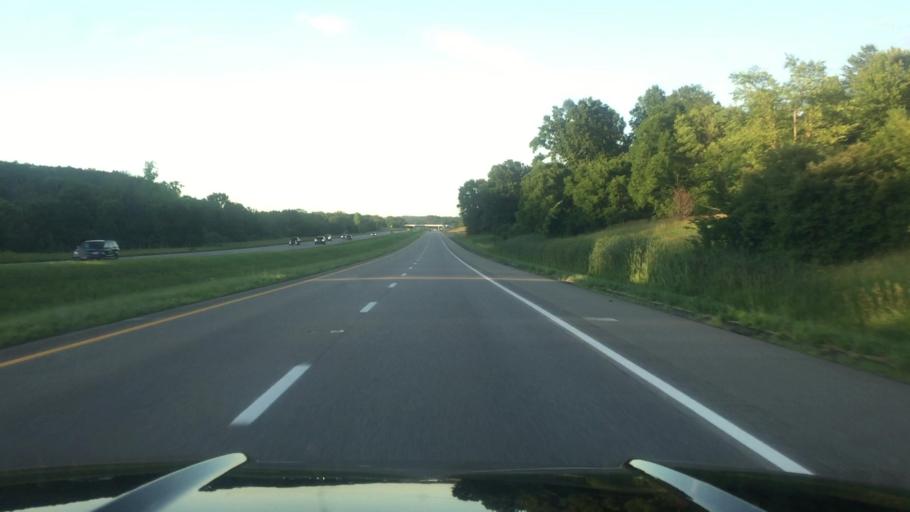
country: US
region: Ohio
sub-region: Tuscarawas County
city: Strasburg
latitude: 40.6188
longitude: -81.4733
